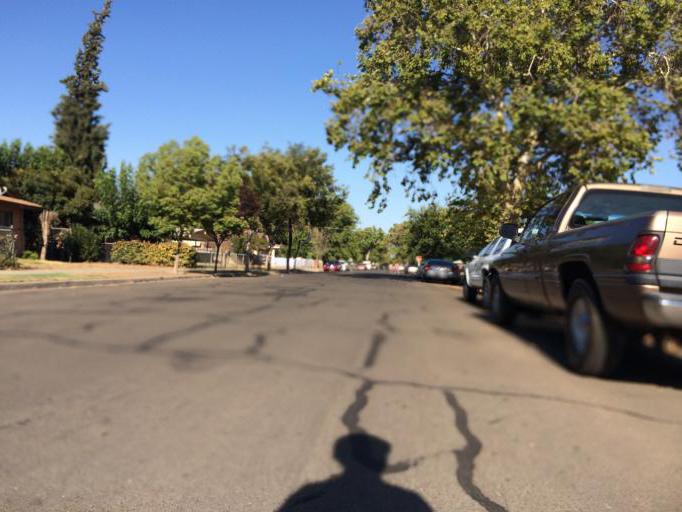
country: US
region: California
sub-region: Fresno County
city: Fresno
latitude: 36.7441
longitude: -119.7655
